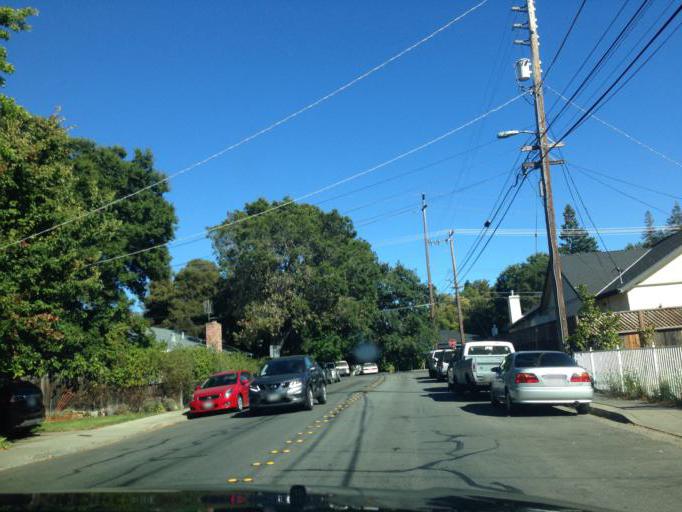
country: US
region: California
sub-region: San Mateo County
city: Atherton
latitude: 37.4543
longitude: -122.2230
